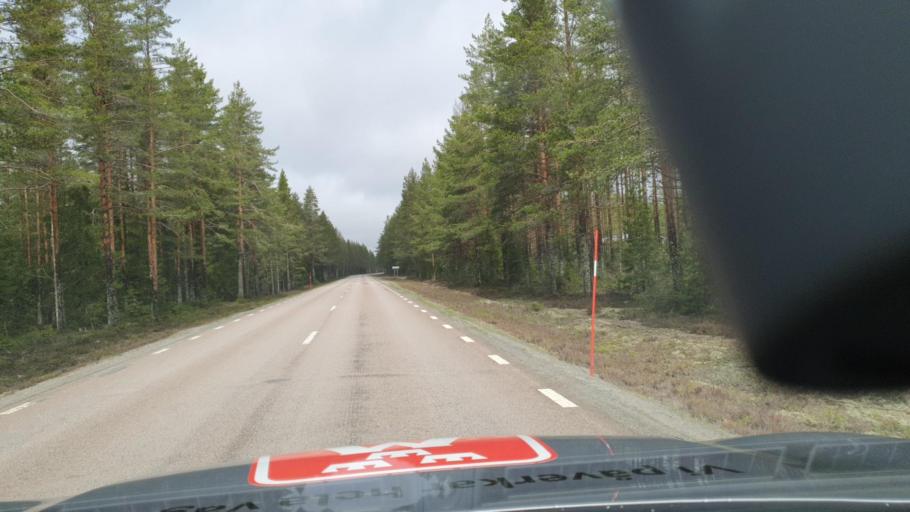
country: SE
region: Vaesternorrland
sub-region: OErnskoeldsviks Kommun
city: Husum
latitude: 63.4235
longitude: 18.9618
